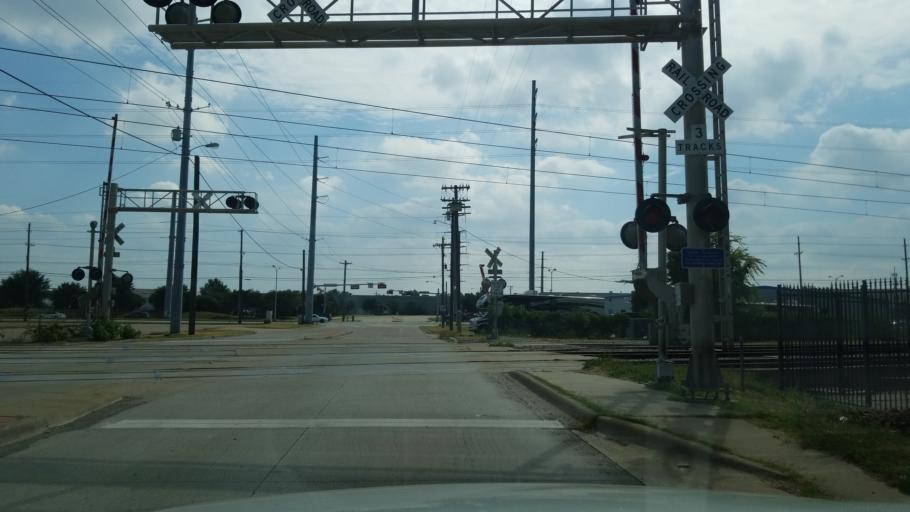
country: US
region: Texas
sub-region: Dallas County
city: Garland
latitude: 32.9103
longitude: -96.6727
